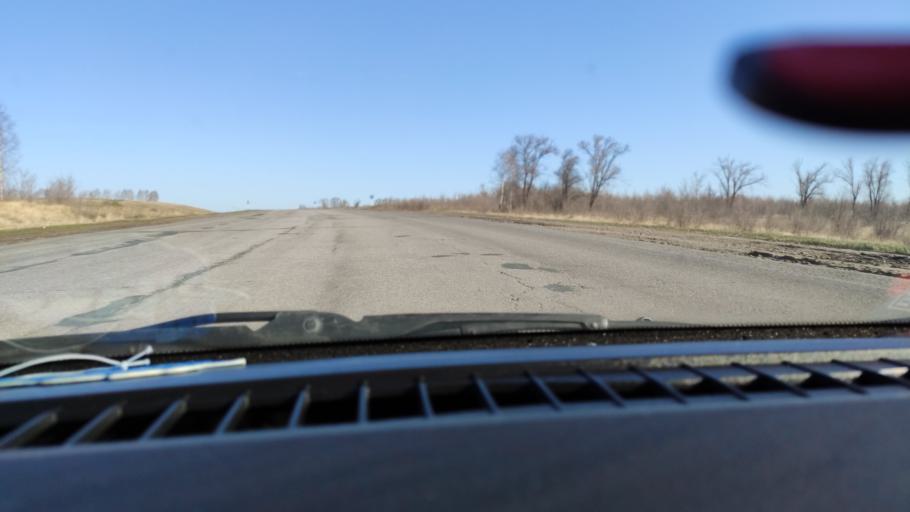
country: RU
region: Samara
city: Varlamovo
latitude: 53.1068
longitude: 48.3567
